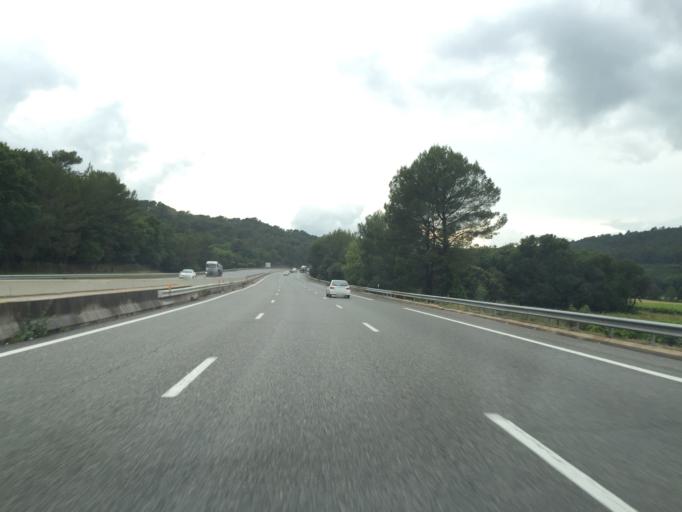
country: FR
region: Provence-Alpes-Cote d'Azur
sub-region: Departement du Var
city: Cabasse
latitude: 43.4064
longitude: 6.1908
